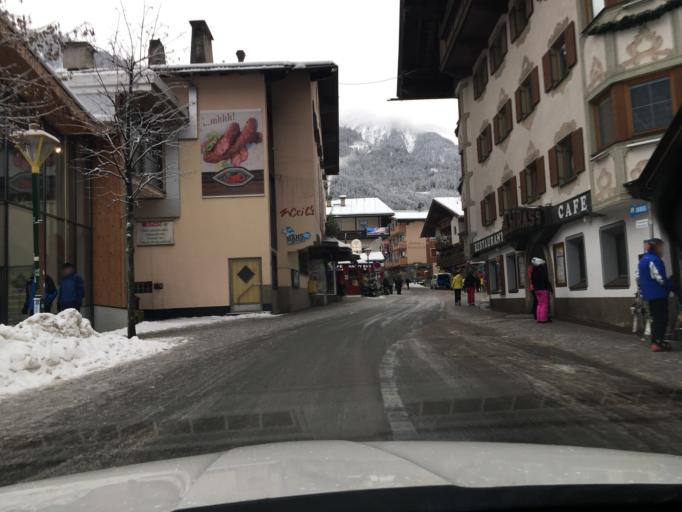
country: AT
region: Tyrol
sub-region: Politischer Bezirk Schwaz
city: Mayrhofen
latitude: 47.1637
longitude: 11.8614
